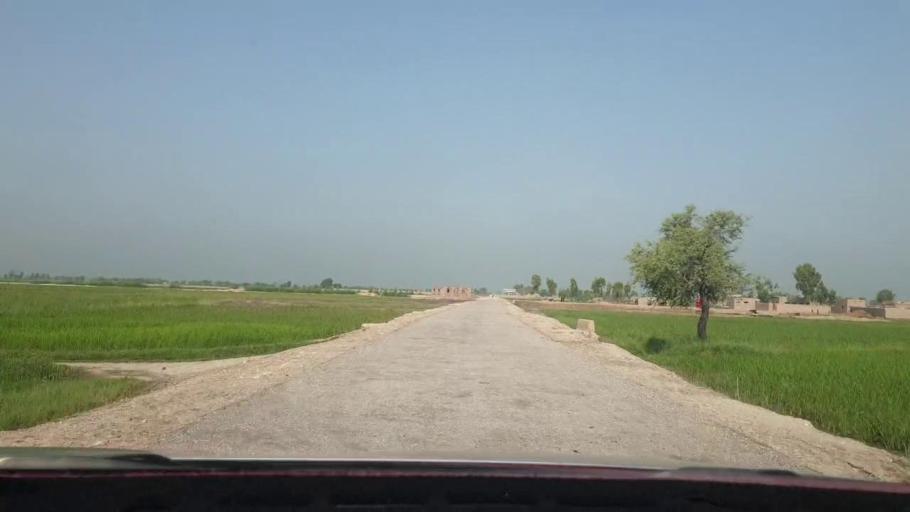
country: PK
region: Sindh
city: Nasirabad
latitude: 27.4351
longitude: 67.9626
